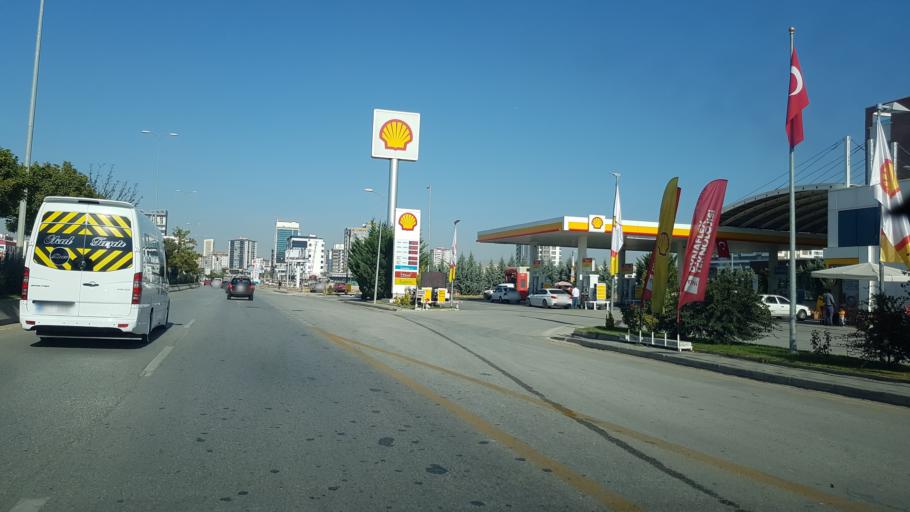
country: TR
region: Ankara
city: Etimesgut
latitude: 39.9623
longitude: 32.6063
